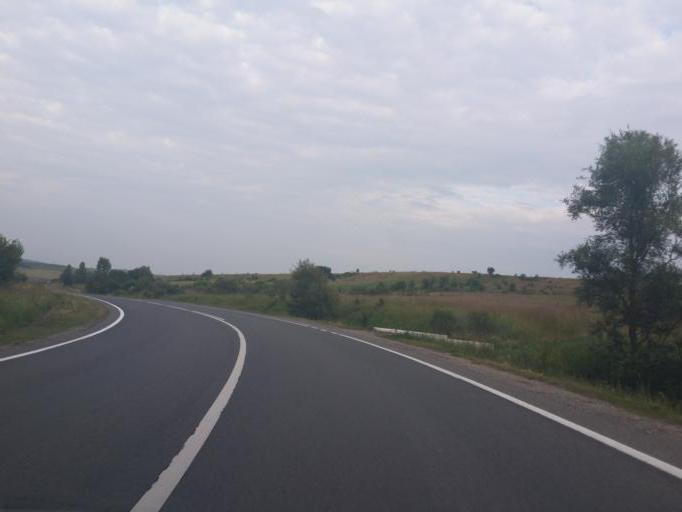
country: RO
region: Cluj
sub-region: Comuna Sanpaul
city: Sanpaul
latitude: 46.9270
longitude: 23.3991
